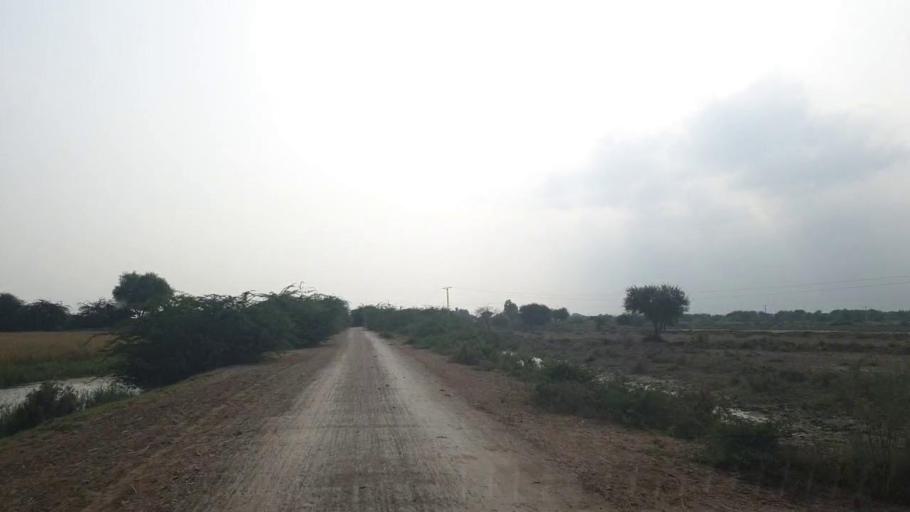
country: PK
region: Sindh
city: Badin
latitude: 24.6242
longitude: 68.6896
